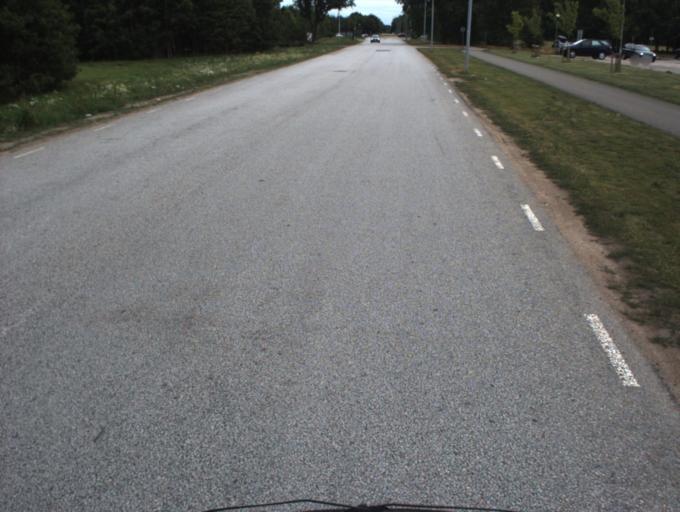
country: SE
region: Skane
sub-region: Helsingborg
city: Helsingborg
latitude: 56.0556
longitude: 12.7351
